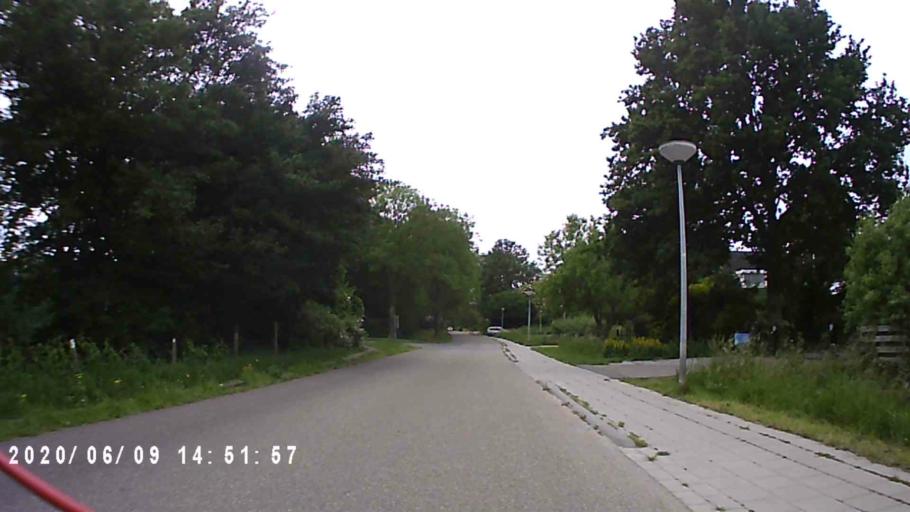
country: NL
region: Groningen
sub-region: Gemeente Winsum
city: Winsum
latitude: 53.3314
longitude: 6.5278
